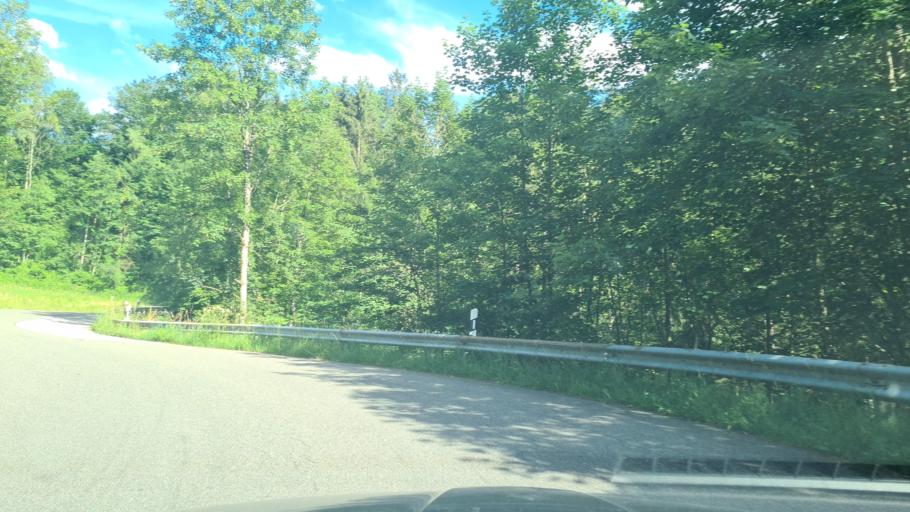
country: AT
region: Salzburg
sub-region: Politischer Bezirk Zell am See
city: Unken
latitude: 47.6689
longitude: 12.7553
